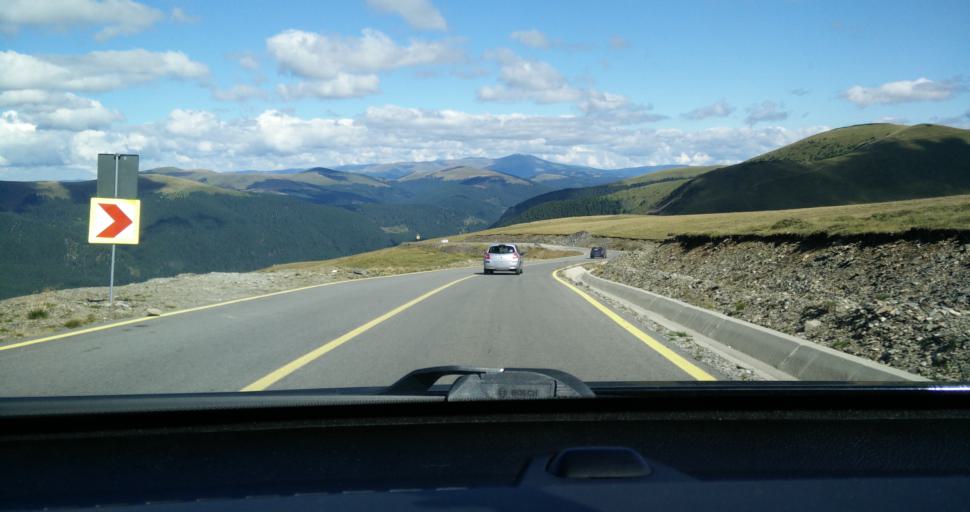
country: RO
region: Gorj
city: Novaci-Straini
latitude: 45.3754
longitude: 23.6539
